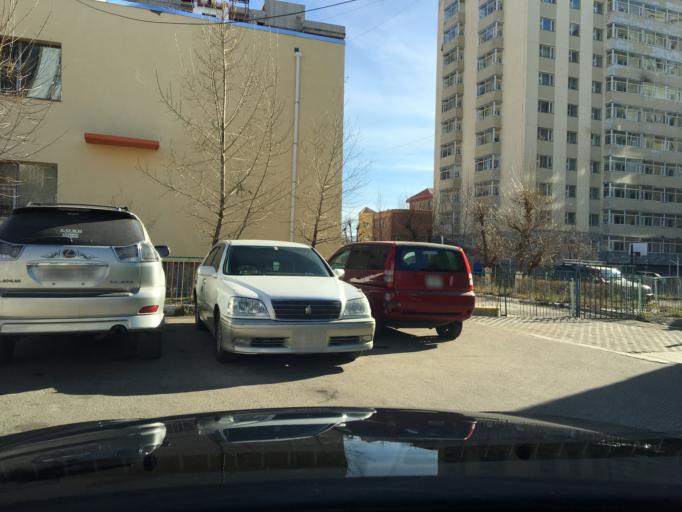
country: MN
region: Ulaanbaatar
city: Ulaanbaatar
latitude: 47.8970
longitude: 106.8941
